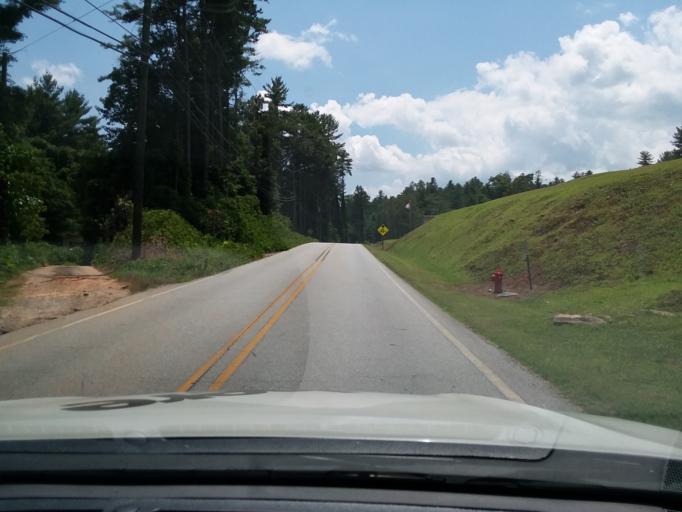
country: US
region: Georgia
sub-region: Rabun County
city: Clayton
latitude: 34.7914
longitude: -83.4161
